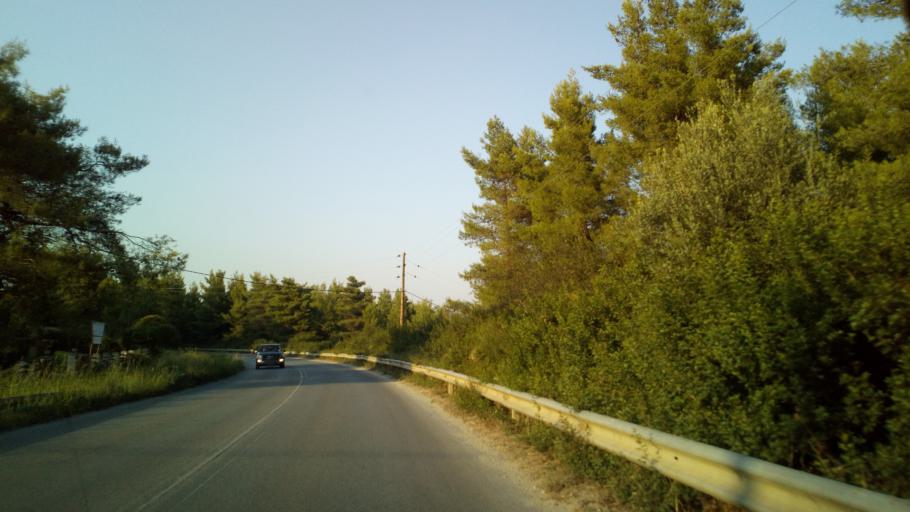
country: GR
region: Central Macedonia
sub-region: Nomos Chalkidikis
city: Pefkochori
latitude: 39.9551
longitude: 23.6737
